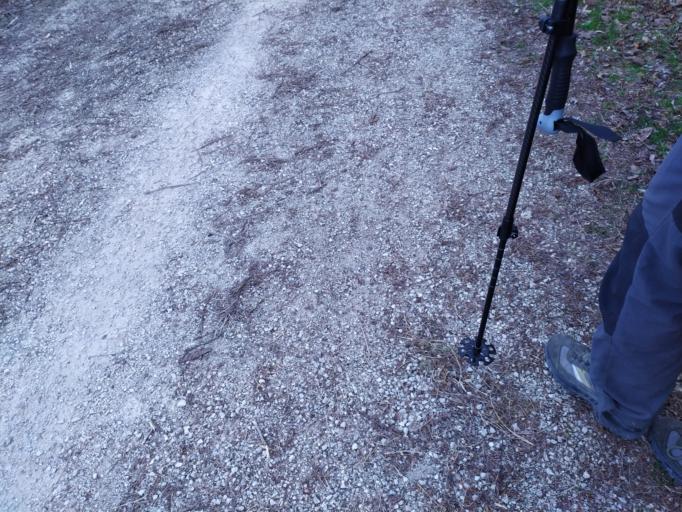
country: IT
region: Veneto
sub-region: Provincia di Vicenza
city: Cogollo del Cengio
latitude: 45.7742
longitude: 11.4109
